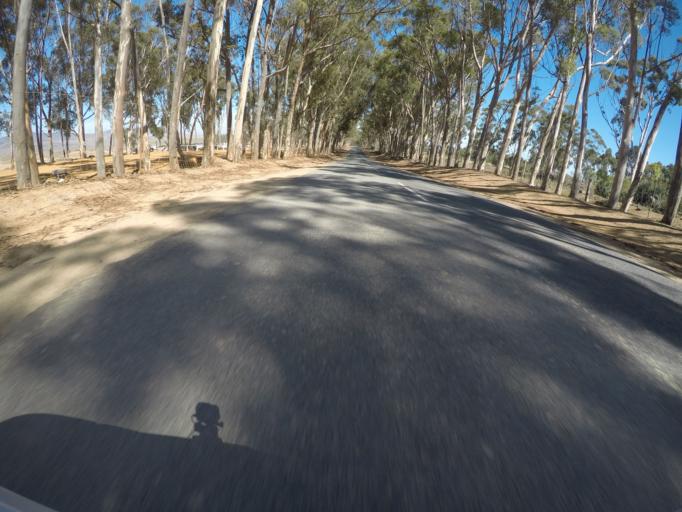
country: ZA
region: Western Cape
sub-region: City of Cape Town
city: Sunset Beach
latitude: -33.7608
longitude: 18.5529
